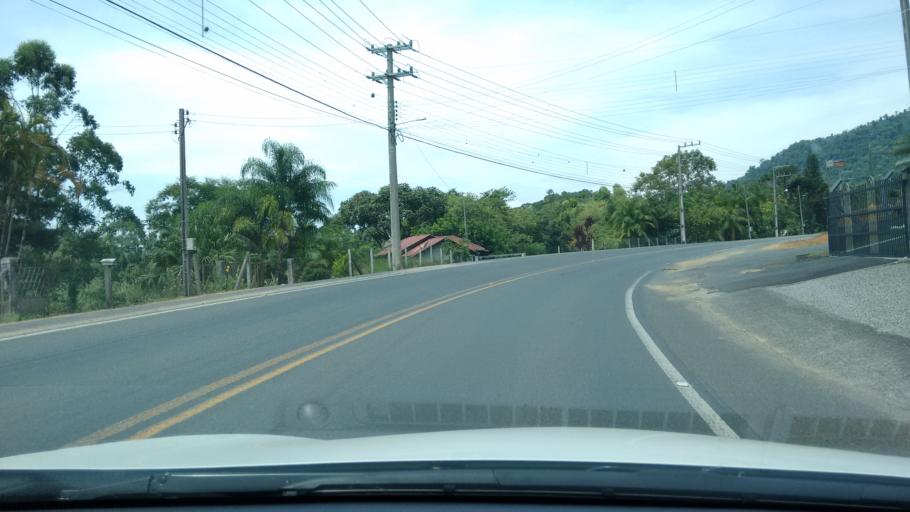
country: BR
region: Santa Catarina
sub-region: Timbo
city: Timbo
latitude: -26.8298
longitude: -49.3175
